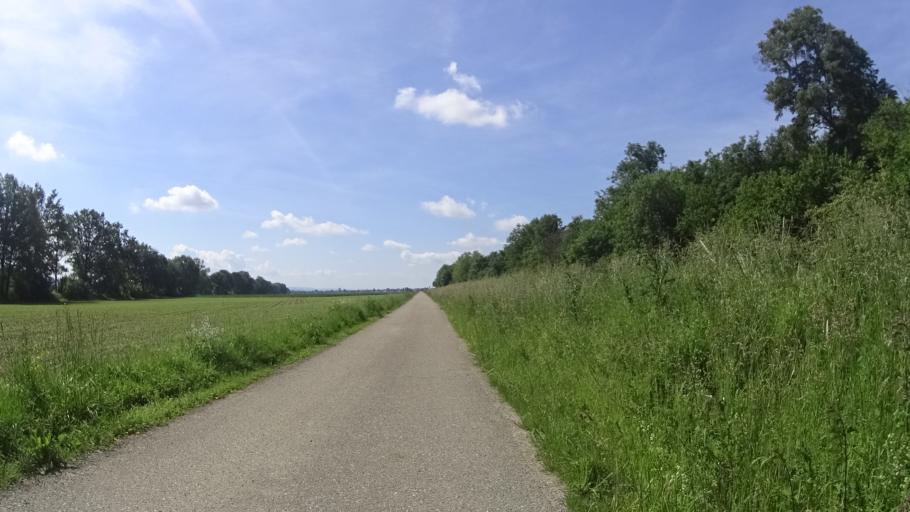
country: DE
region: Baden-Wuerttemberg
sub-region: Freiburg Region
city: Schutterwald
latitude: 48.4880
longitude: 7.8179
